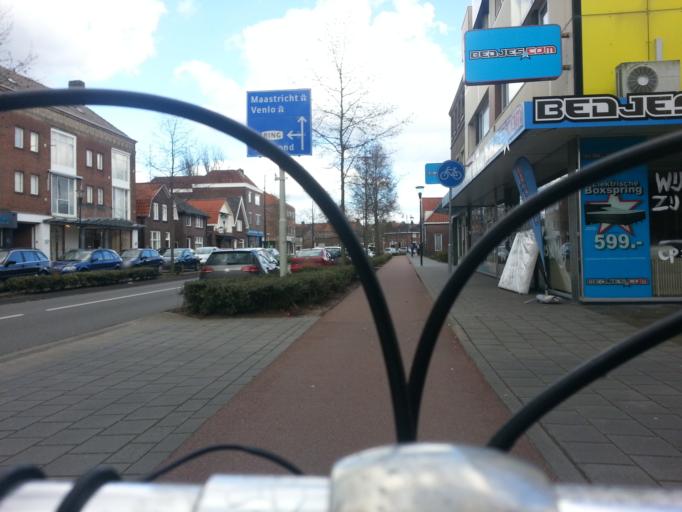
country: NL
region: North Brabant
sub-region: Gemeente Eindhoven
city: Lakerlopen
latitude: 51.4254
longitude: 5.4905
